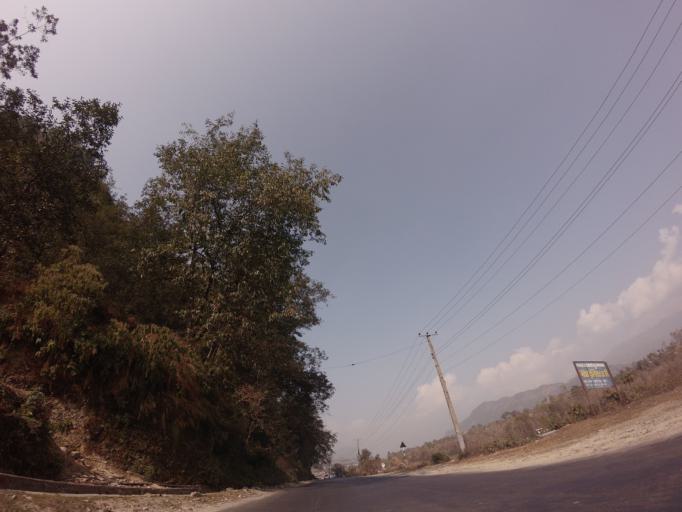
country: NP
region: Western Region
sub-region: Gandaki Zone
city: Pokhara
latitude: 28.2492
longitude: 83.9733
